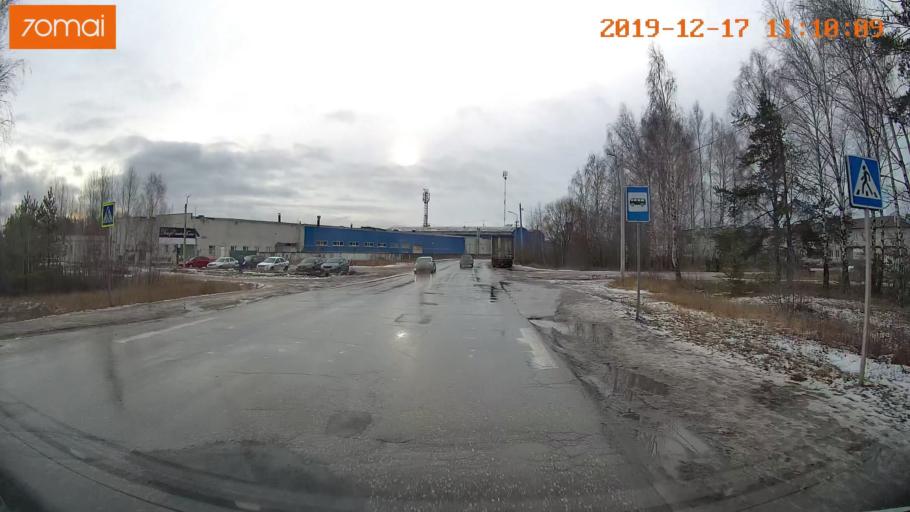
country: RU
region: Vladimir
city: Gus'-Khrustal'nyy
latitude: 55.5950
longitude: 40.6421
